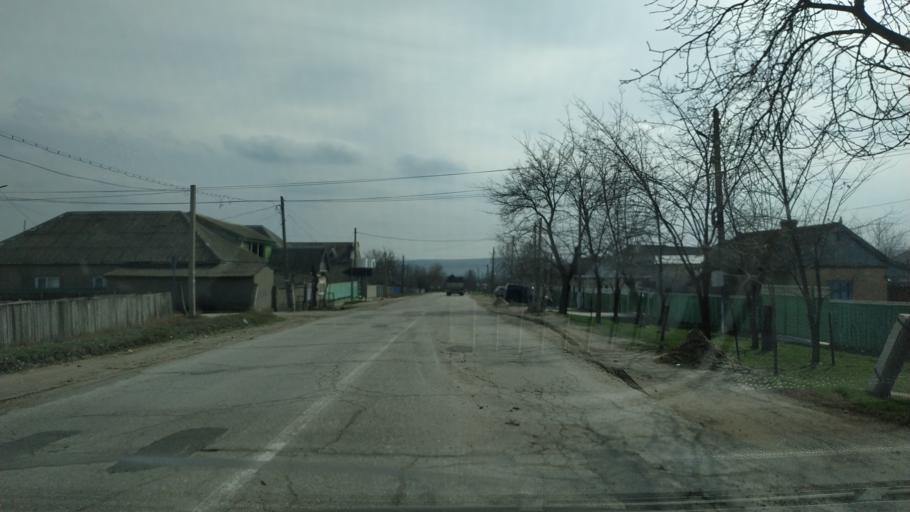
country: MD
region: Gagauzia
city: Vulcanesti
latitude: 45.6949
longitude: 28.4044
